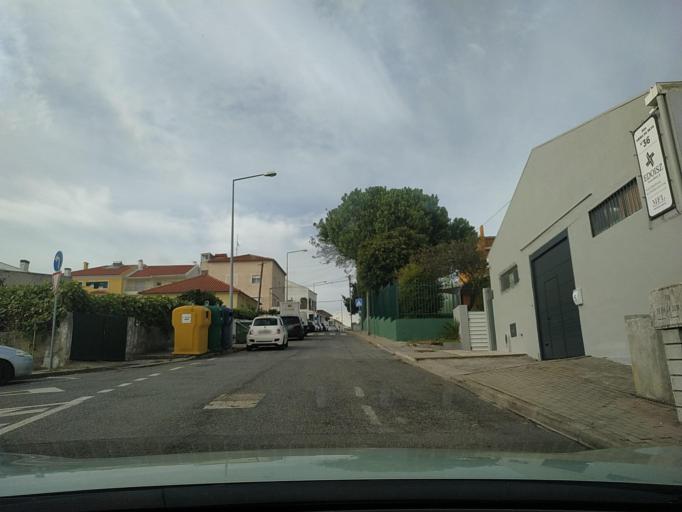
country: PT
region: Lisbon
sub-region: Amadora
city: Amadora
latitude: 38.7760
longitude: -9.2337
